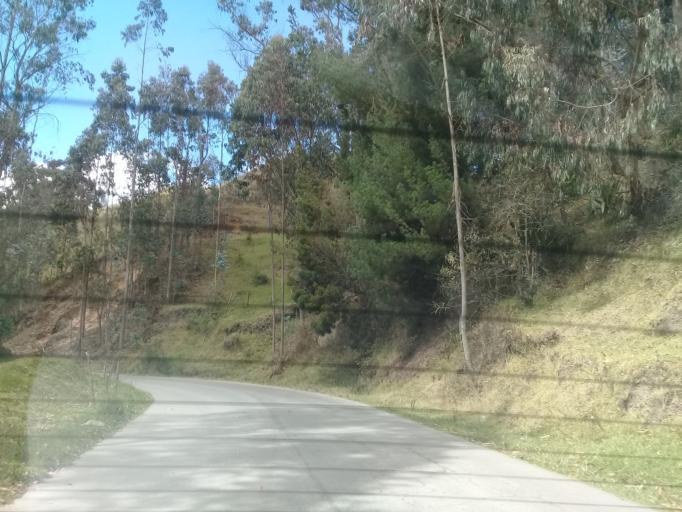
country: CO
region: Cundinamarca
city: Choconta
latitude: 5.1512
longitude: -73.6999
